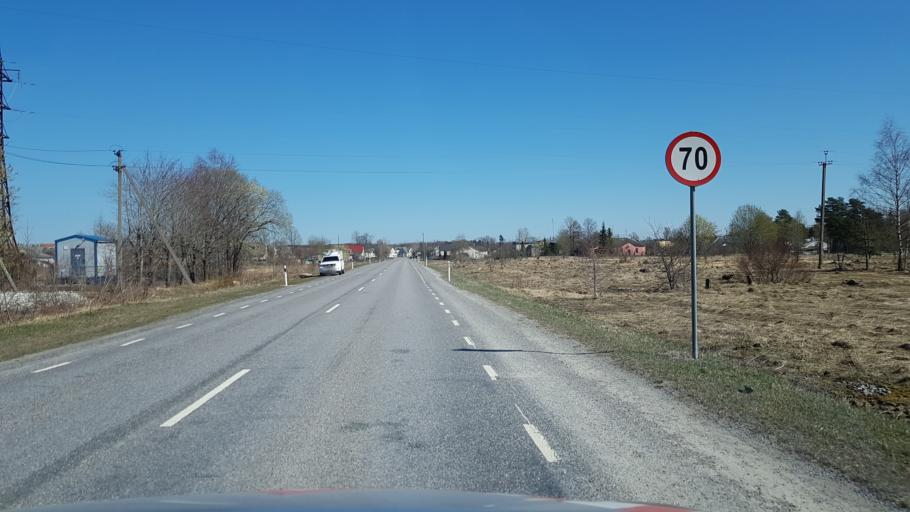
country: EE
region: Ida-Virumaa
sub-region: Kohtla-Jaerve linn
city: Kohtla-Jarve
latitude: 59.3339
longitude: 27.2810
